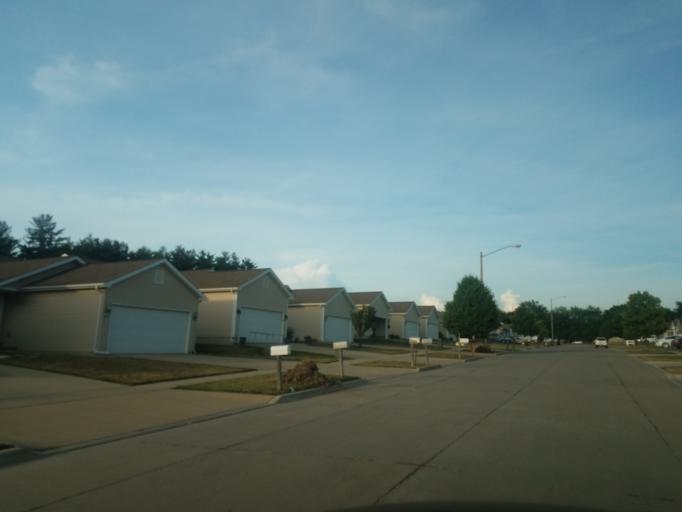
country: US
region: Illinois
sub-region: McLean County
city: Bloomington
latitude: 40.4491
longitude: -89.0097
